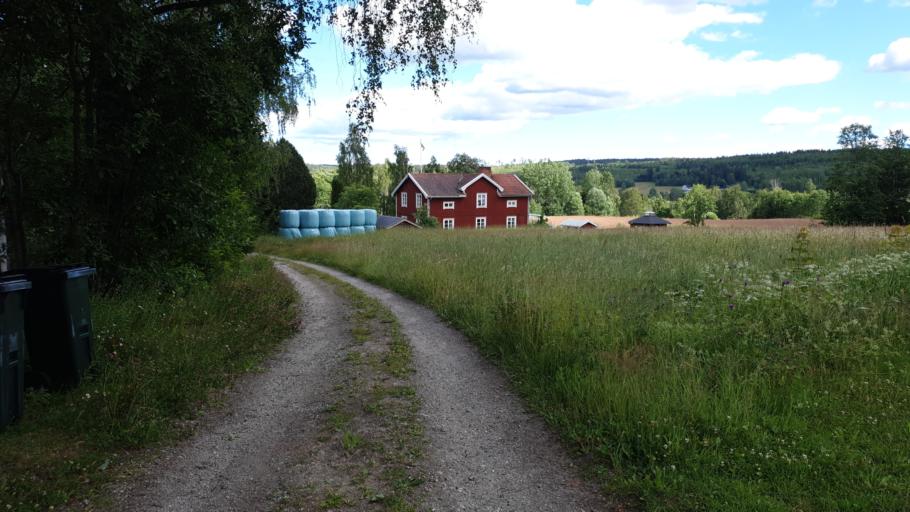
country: SE
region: Gaevleborg
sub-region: Nordanstigs Kommun
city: Bergsjoe
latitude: 62.0401
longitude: 17.0881
